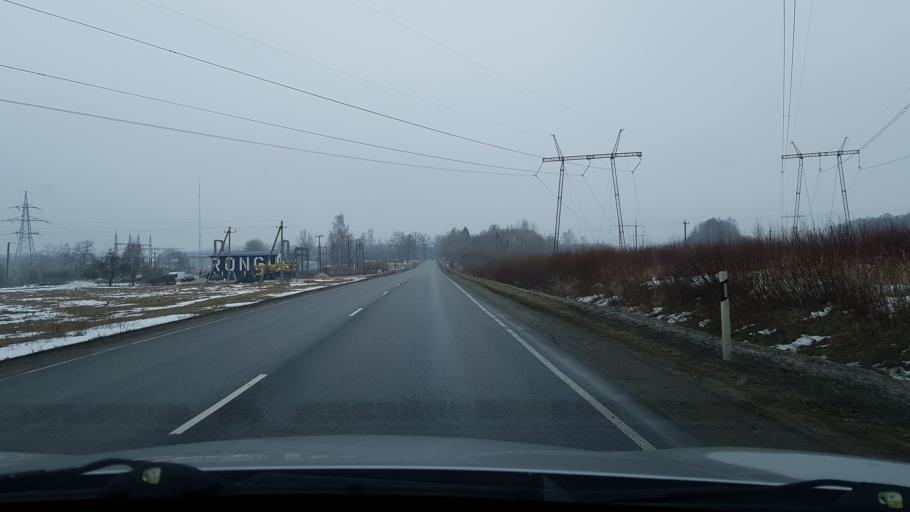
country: EE
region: Tartu
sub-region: Elva linn
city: Elva
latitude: 58.1329
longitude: 26.2453
